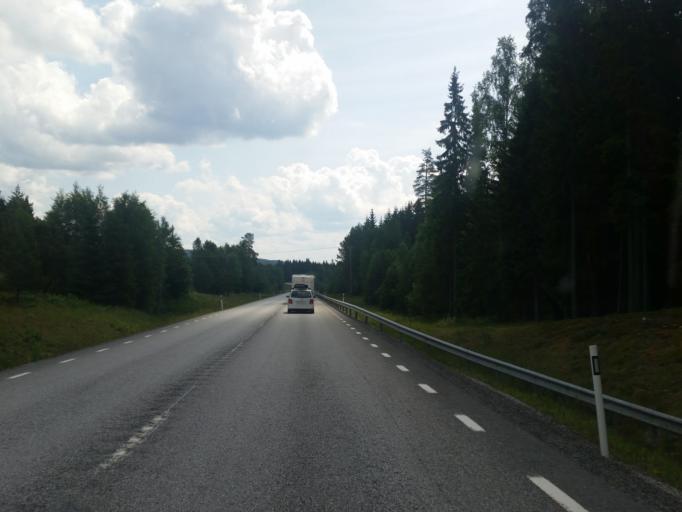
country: SE
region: OErebro
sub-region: Ljusnarsbergs Kommun
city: Kopparberg
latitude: 59.8783
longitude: 15.0327
